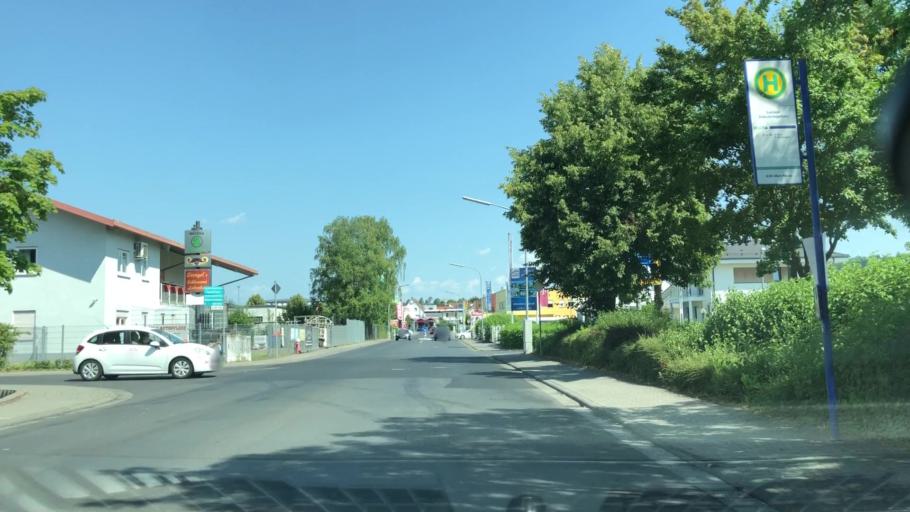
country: DE
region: Hesse
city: Hain-Grundau
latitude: 50.2040
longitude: 9.1369
